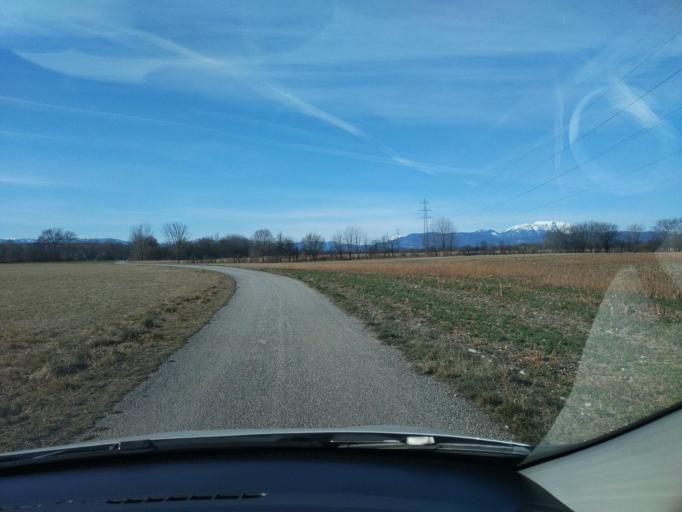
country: AT
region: Lower Austria
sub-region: Politischer Bezirk Wiener Neustadt
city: Bad Erlach
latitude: 47.7390
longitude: 16.1944
